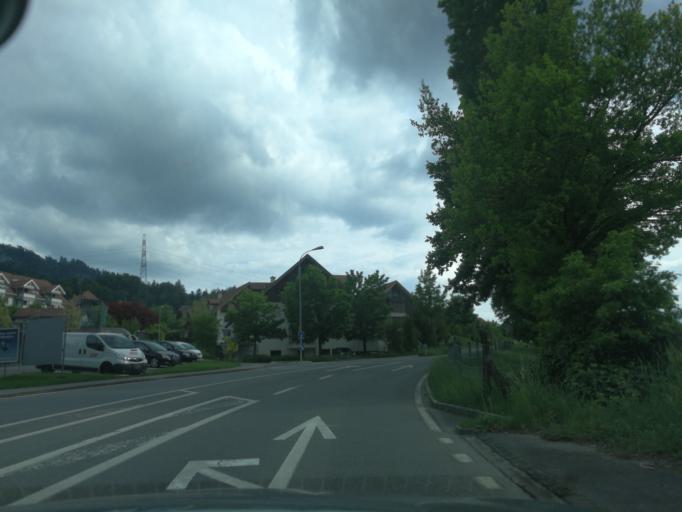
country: CH
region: Lucerne
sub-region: Entlebuch District
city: Oberdiessbach
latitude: 46.8350
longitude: 7.6230
